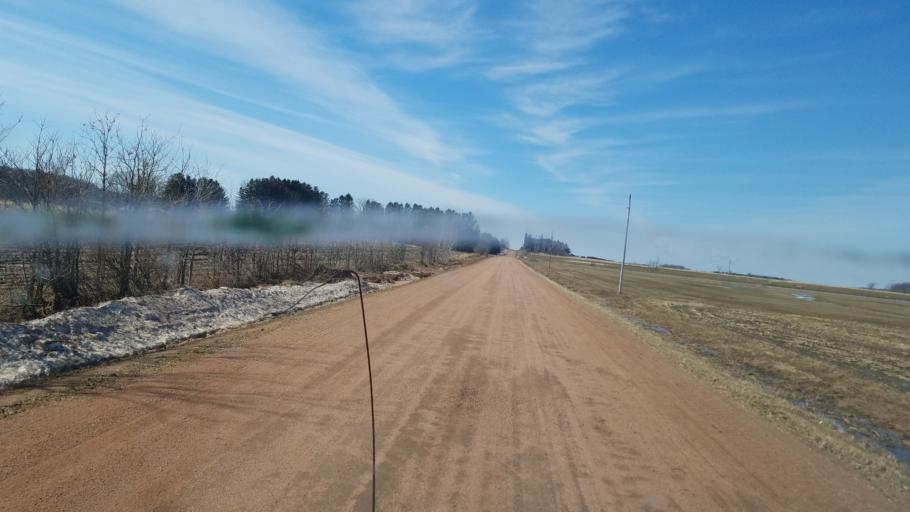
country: US
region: Wisconsin
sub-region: Clark County
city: Loyal
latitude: 44.6111
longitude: -90.4312
